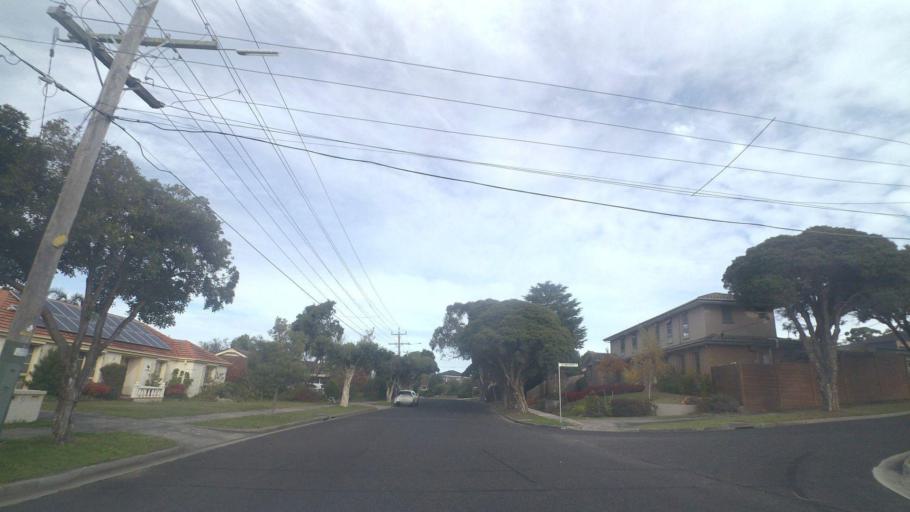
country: AU
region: Victoria
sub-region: Whitehorse
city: Vermont South
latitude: -37.8584
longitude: 145.1881
